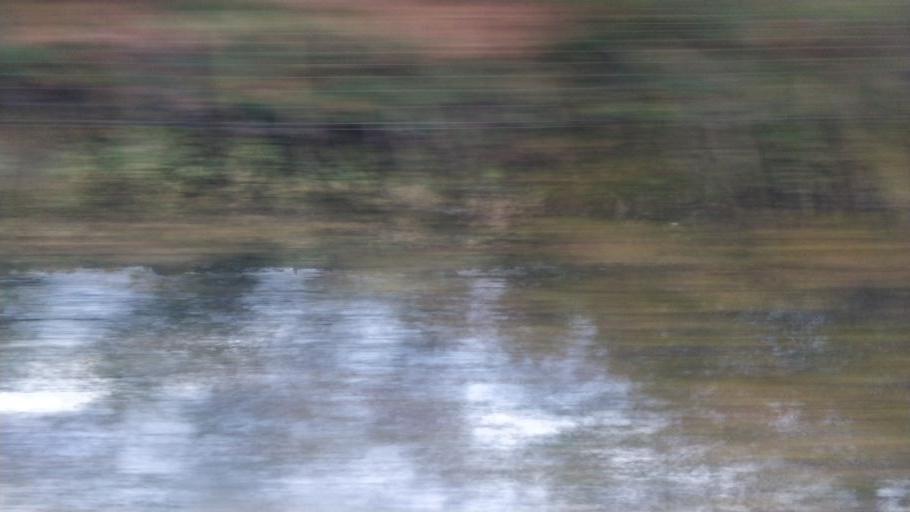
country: GB
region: England
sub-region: Lancashire
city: Banks
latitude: 53.6282
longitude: -2.9310
